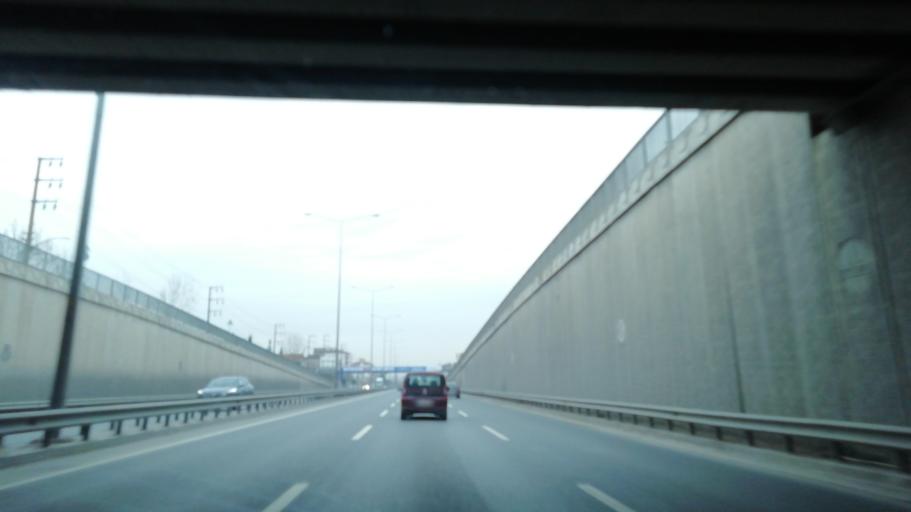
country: TR
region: Kocaeli
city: Derince
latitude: 40.7563
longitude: 29.8205
